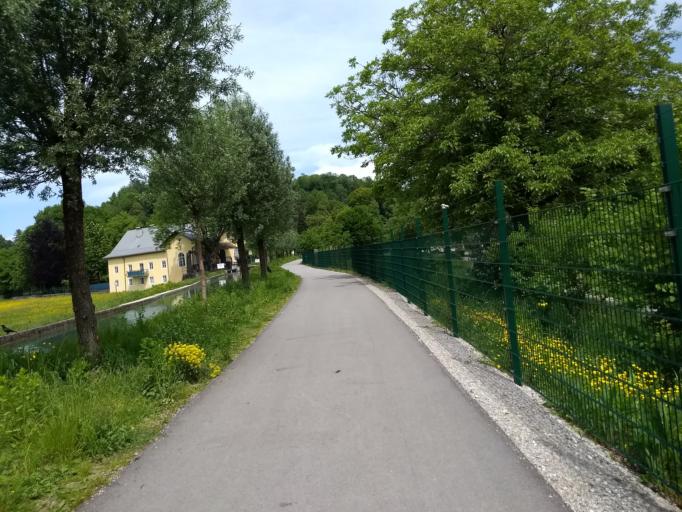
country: AT
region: Salzburg
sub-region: Salzburg Stadt
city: Salzburg
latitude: 47.7891
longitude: 13.0419
